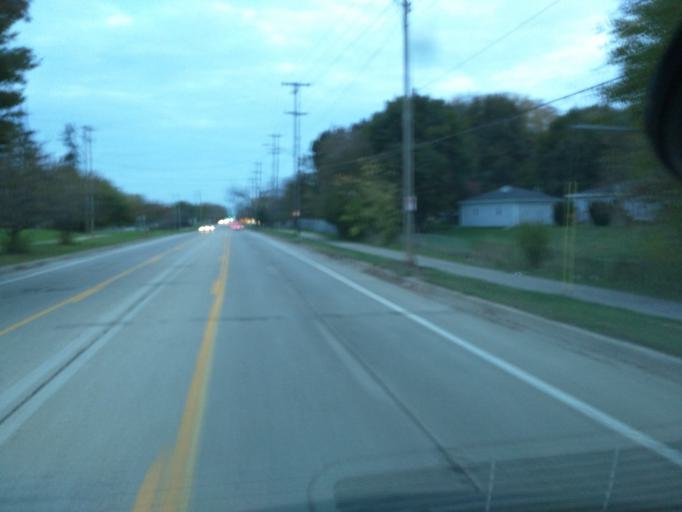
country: US
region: Michigan
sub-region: Eaton County
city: Waverly
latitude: 42.6869
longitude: -84.6031
